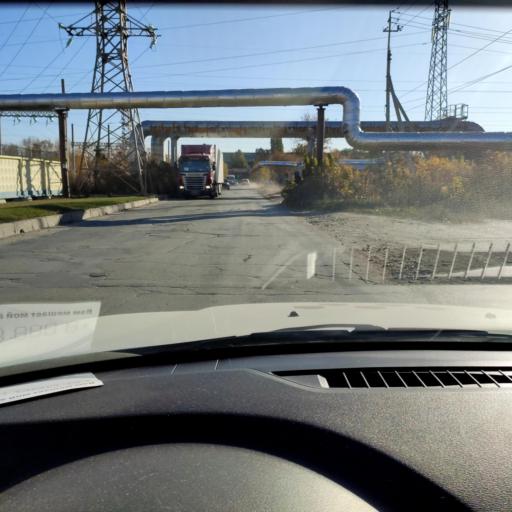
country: RU
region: Samara
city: Tol'yatti
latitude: 53.5451
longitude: 49.4416
